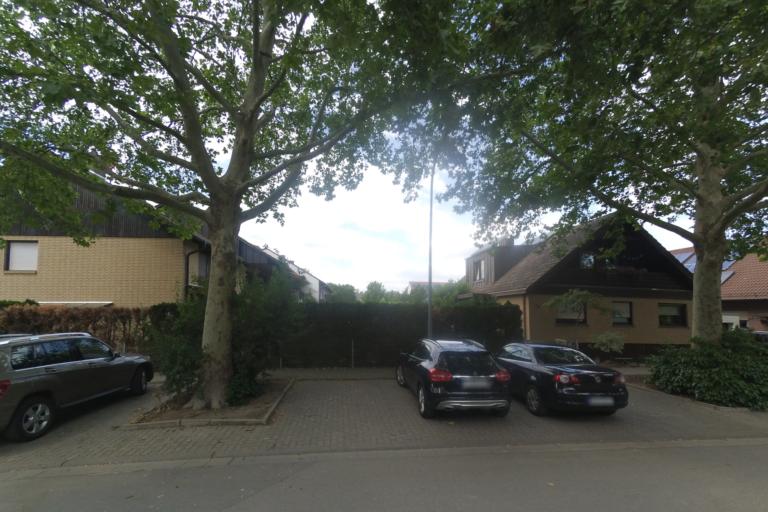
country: DE
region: Rheinland-Pfalz
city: Frankenthal
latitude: 49.5164
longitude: 8.3372
